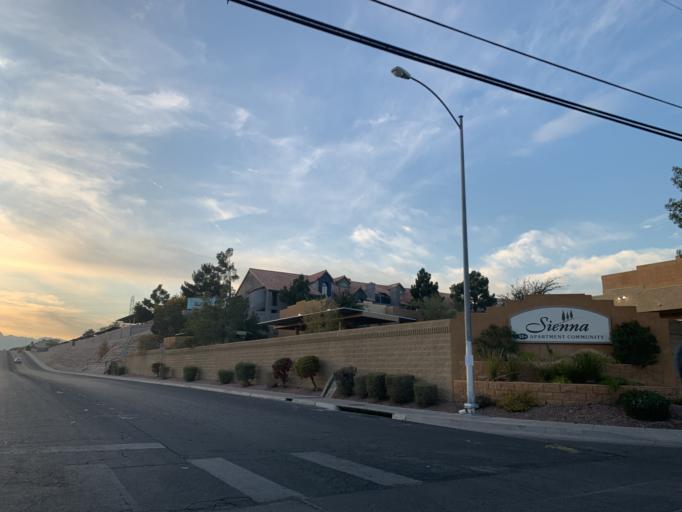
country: US
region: Nevada
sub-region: Clark County
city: Spring Valley
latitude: 36.1118
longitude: -115.2082
